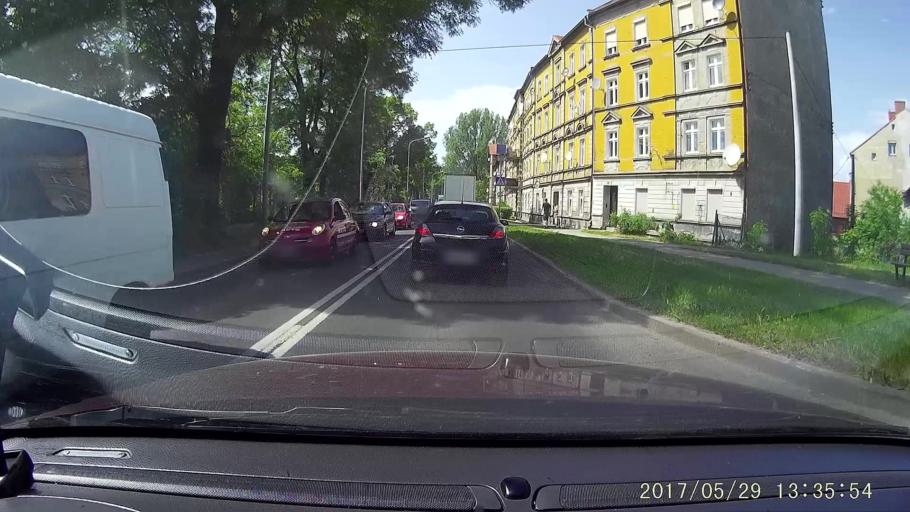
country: PL
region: Lower Silesian Voivodeship
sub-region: Powiat lubanski
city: Luban
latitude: 51.1112
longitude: 15.2965
